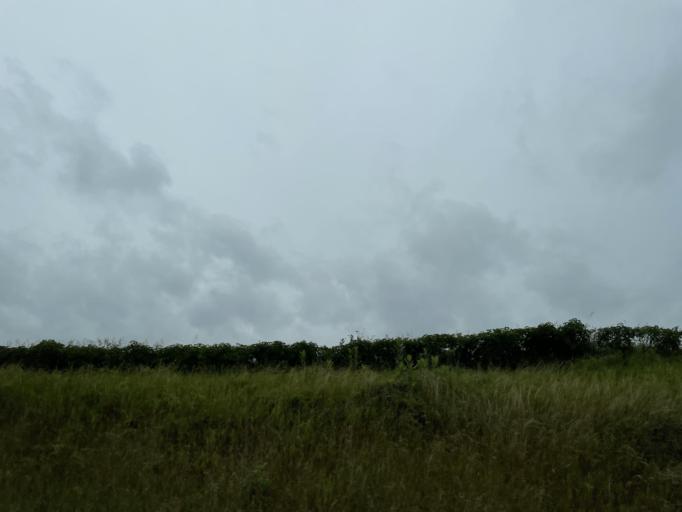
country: CA
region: Ontario
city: Cambridge
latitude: 43.4404
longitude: -80.2645
